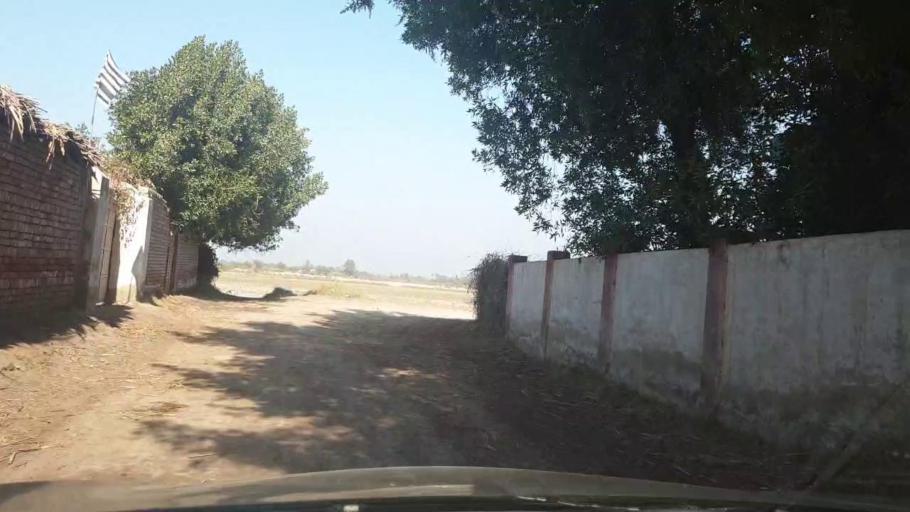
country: PK
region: Sindh
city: Ubauro
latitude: 28.1456
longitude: 69.6976
